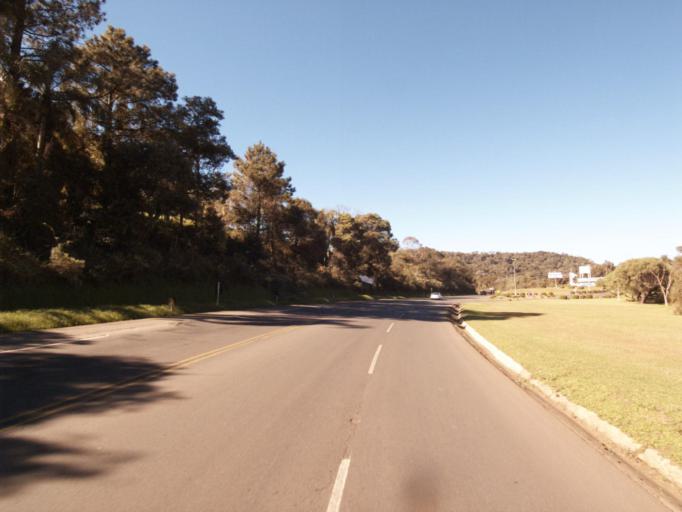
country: BR
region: Santa Catarina
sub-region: Chapeco
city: Chapeco
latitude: -26.9959
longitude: -52.6383
